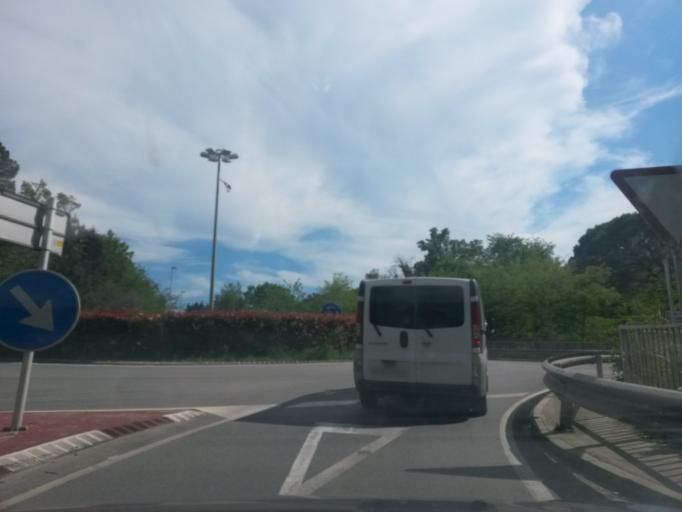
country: ES
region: Catalonia
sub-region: Provincia de Girona
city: Angles
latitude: 41.9502
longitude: 2.6406
